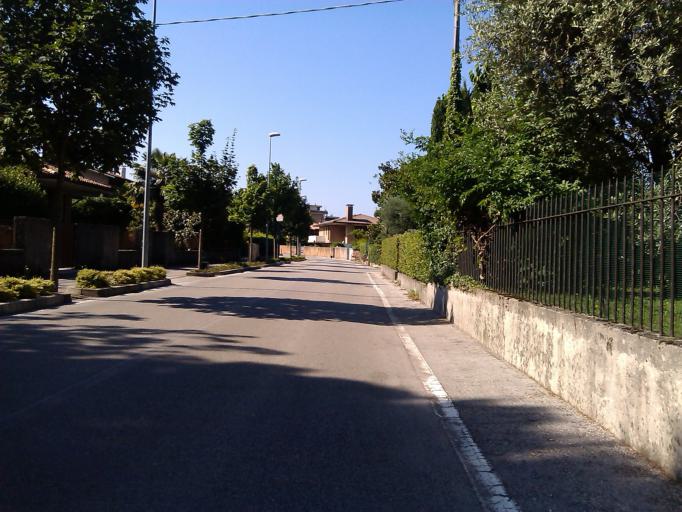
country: IT
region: Veneto
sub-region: Provincia di Vicenza
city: Bassano del Grappa
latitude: 45.7744
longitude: 11.7448
